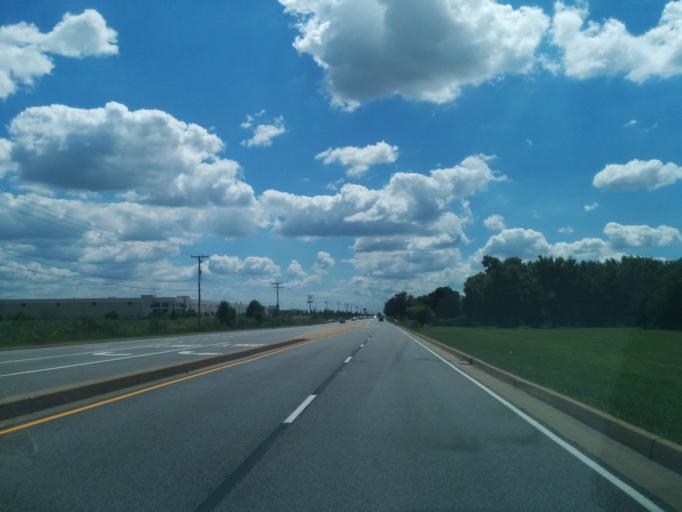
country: US
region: Illinois
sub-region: Will County
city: Romeoville
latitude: 41.6819
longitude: -88.1258
